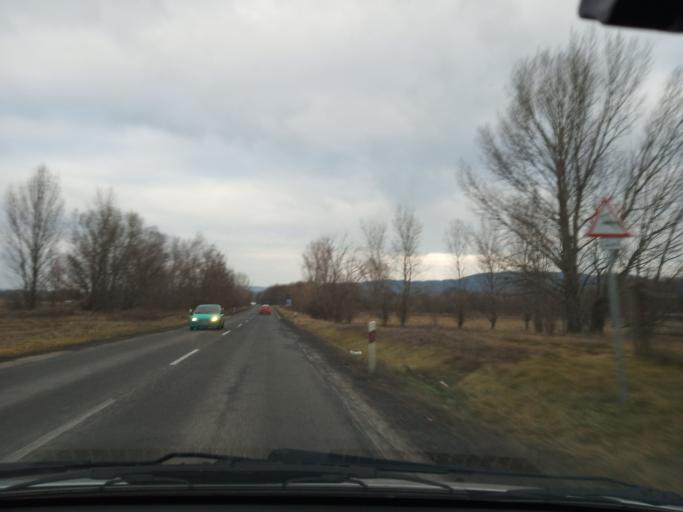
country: HU
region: Komarom-Esztergom
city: Dorog
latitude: 47.7566
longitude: 18.7343
